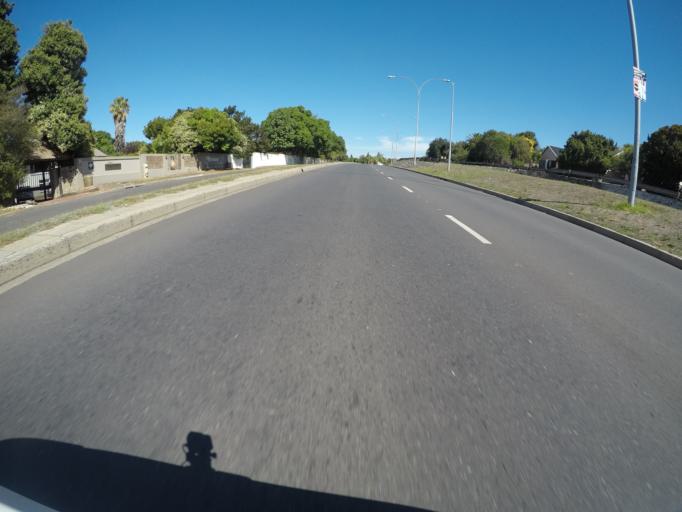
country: ZA
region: Western Cape
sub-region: City of Cape Town
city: Kraaifontein
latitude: -33.8409
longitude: 18.6482
